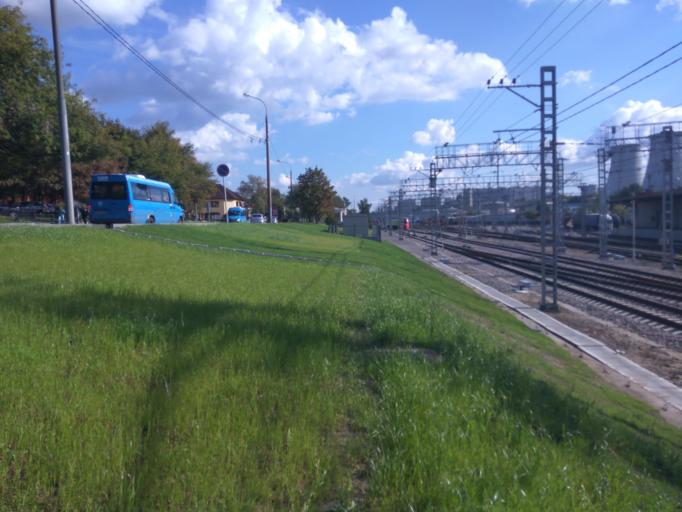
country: RU
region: Moscow
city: Novyye Cheremushki
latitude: 55.7042
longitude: 37.5895
